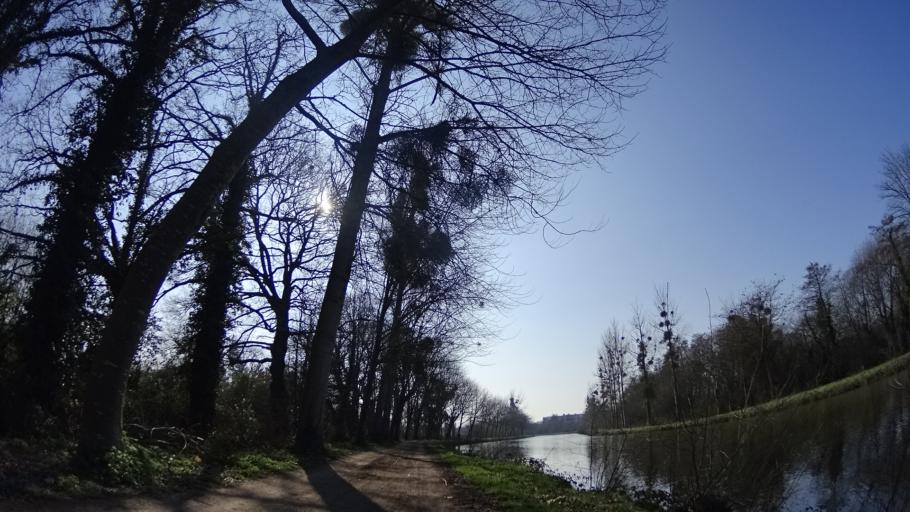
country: FR
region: Brittany
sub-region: Departement d'Ille-et-Vilaine
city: Saint-Gregoire
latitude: 48.1363
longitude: -1.6762
